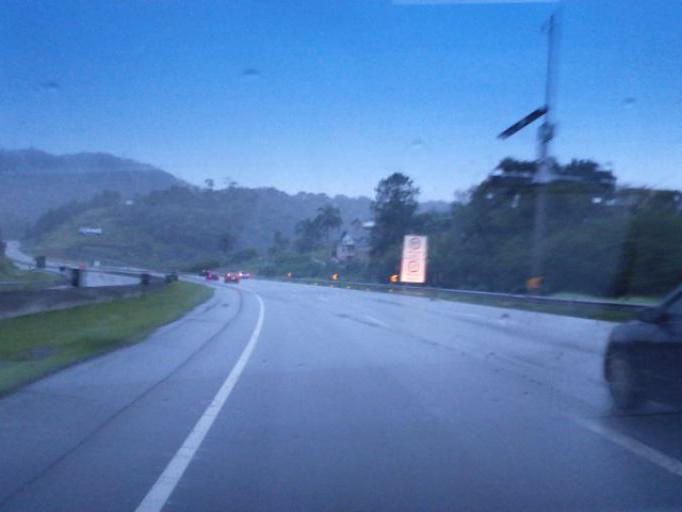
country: BR
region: Sao Paulo
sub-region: Juquitiba
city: Juquitiba
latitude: -24.0088
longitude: -47.1603
